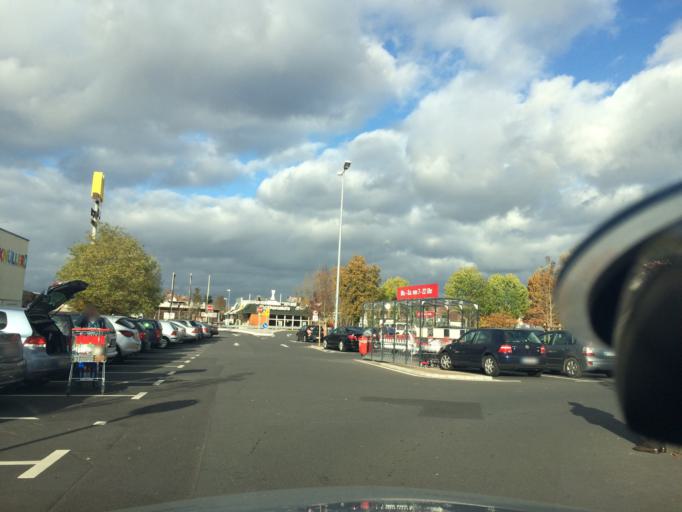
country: DE
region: Hesse
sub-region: Regierungsbezirk Darmstadt
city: Egelsbach
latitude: 49.9621
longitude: 8.6728
